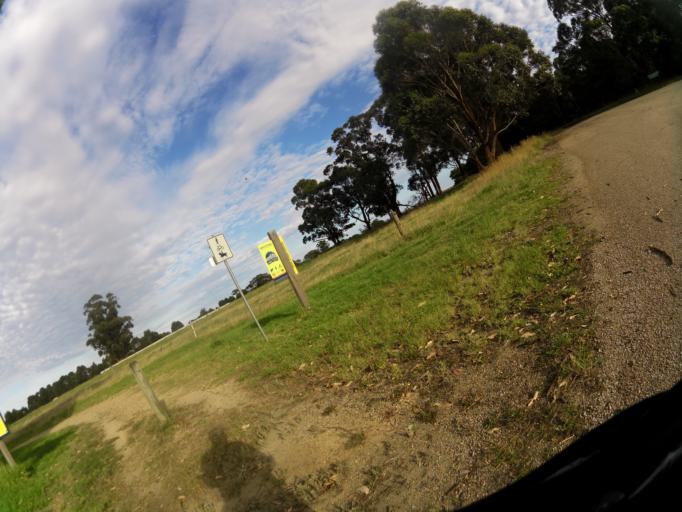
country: AU
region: Victoria
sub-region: East Gippsland
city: Lakes Entrance
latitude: -37.7161
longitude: 148.4525
